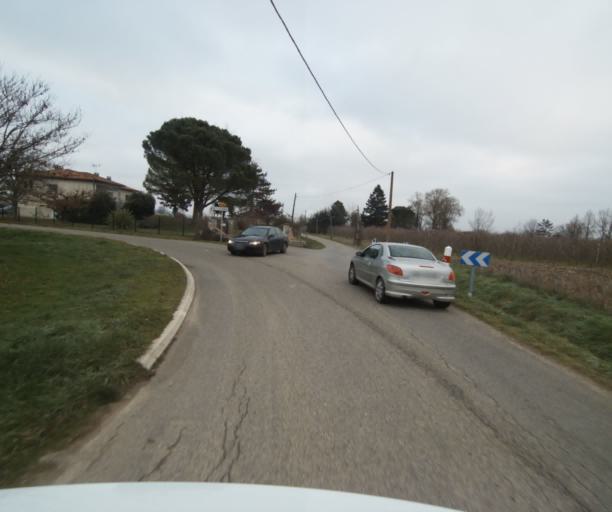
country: FR
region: Midi-Pyrenees
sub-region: Departement du Tarn-et-Garonne
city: Moissac
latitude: 44.1039
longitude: 1.1266
